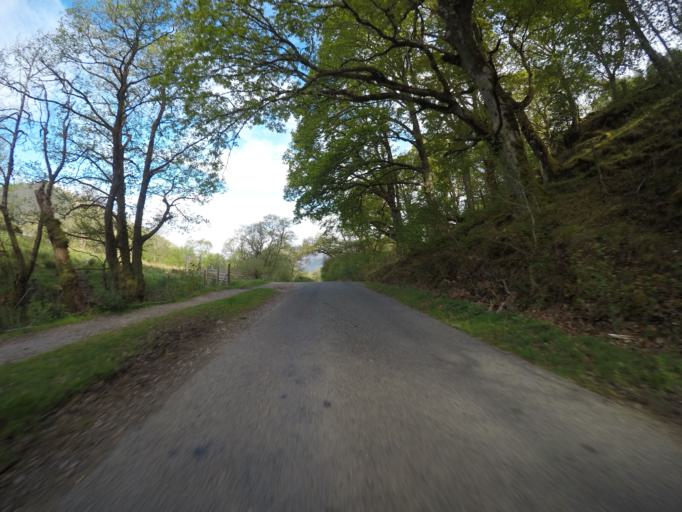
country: GB
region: Scotland
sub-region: Highland
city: Fort William
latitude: 56.6767
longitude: -5.0790
